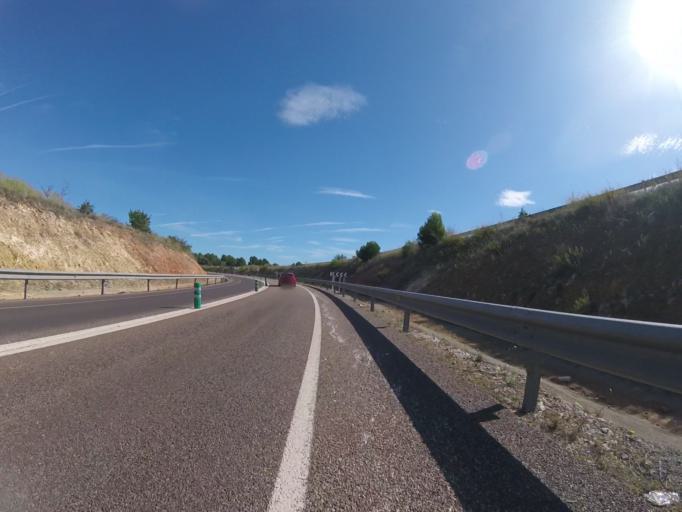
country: ES
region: Valencia
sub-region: Provincia de Castello
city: Peniscola
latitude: 40.3932
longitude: 0.3589
